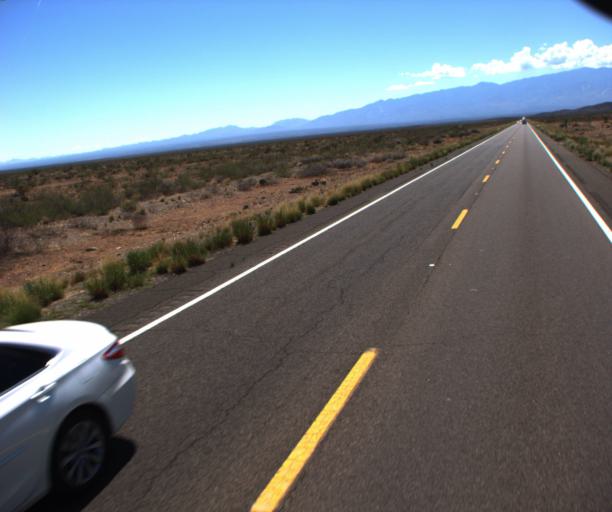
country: US
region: Arizona
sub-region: Graham County
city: Safford
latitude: 32.8239
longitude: -109.4680
